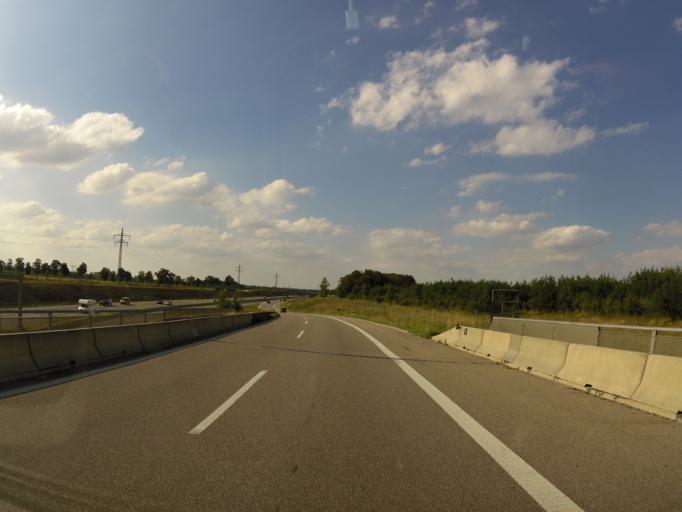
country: DE
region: Bavaria
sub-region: Upper Bavaria
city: Germering
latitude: 48.1287
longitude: 11.4035
